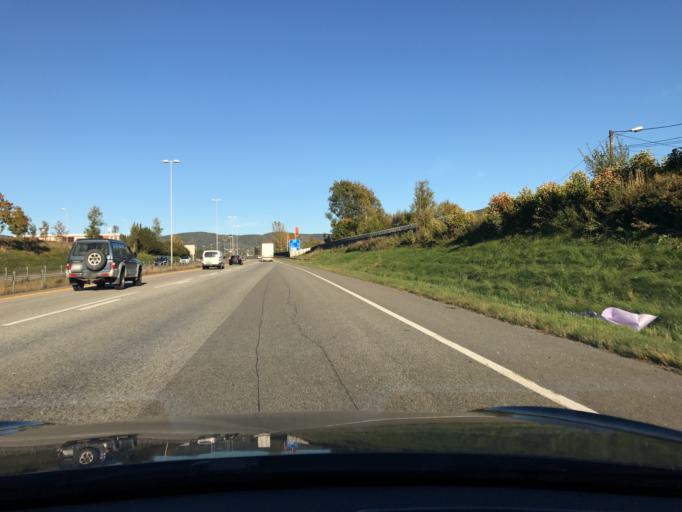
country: NO
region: Buskerud
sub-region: Drammen
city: Drammen
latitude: 59.7483
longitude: 10.2399
